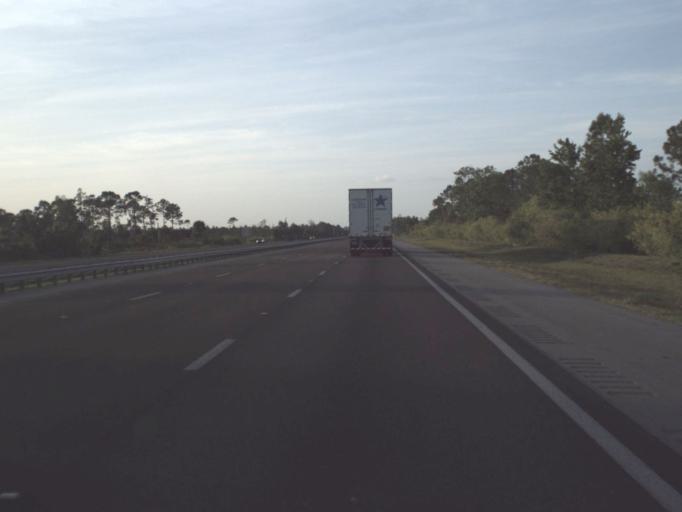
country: US
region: Florida
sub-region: Volusia County
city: Oak Hill
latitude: 28.7804
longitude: -80.8963
